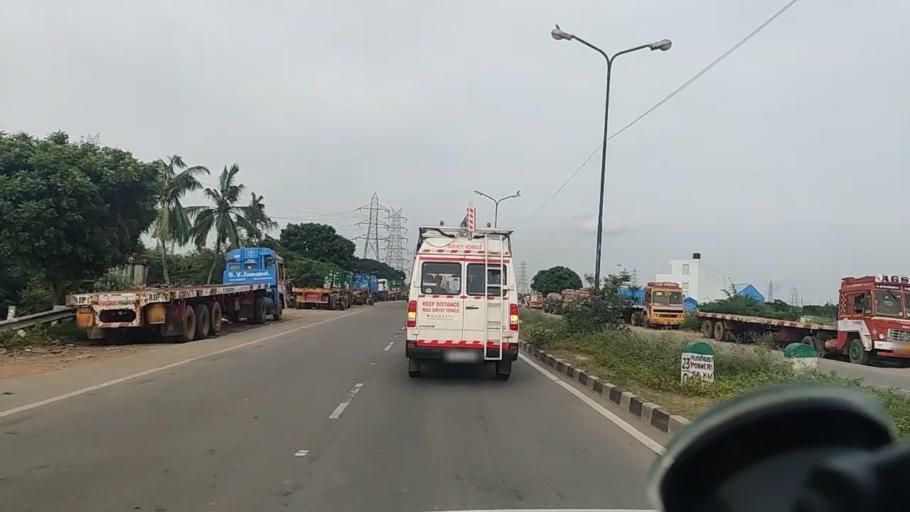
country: IN
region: Tamil Nadu
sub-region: Thiruvallur
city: Chinnasekkadu
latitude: 13.1789
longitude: 80.2510
